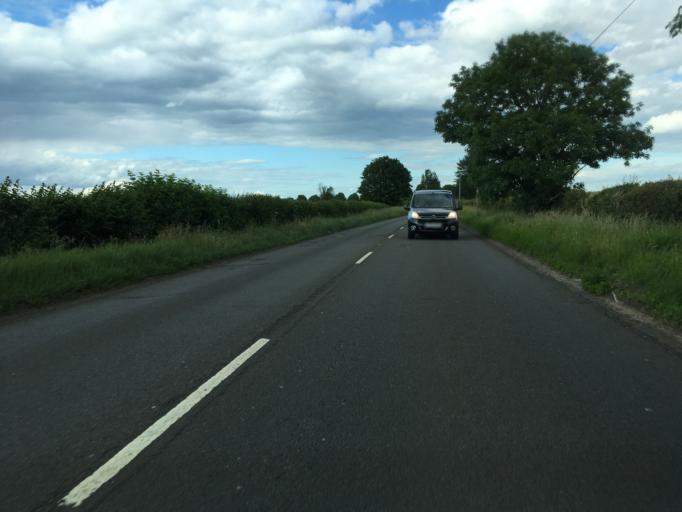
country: GB
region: England
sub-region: Oxfordshire
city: Thame
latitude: 51.7684
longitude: -0.9619
